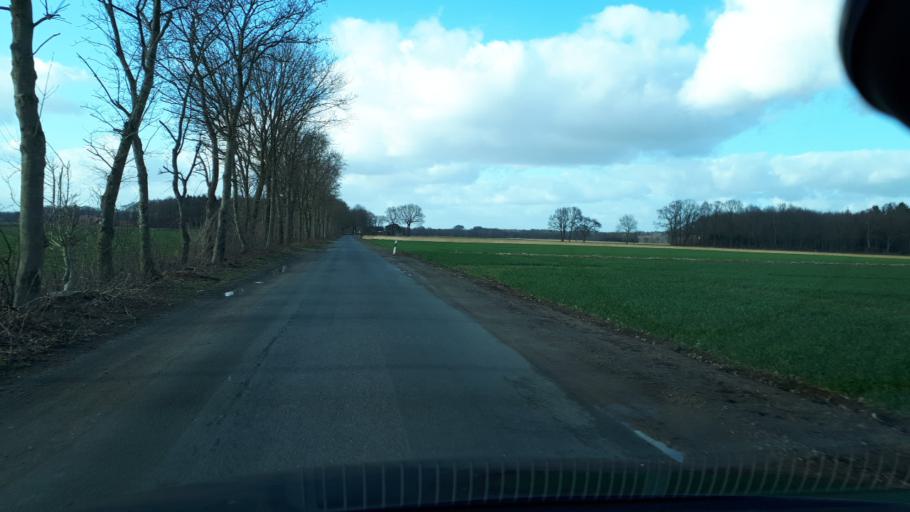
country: DE
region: Lower Saxony
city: Cloppenburg
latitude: 52.8395
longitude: 7.9974
